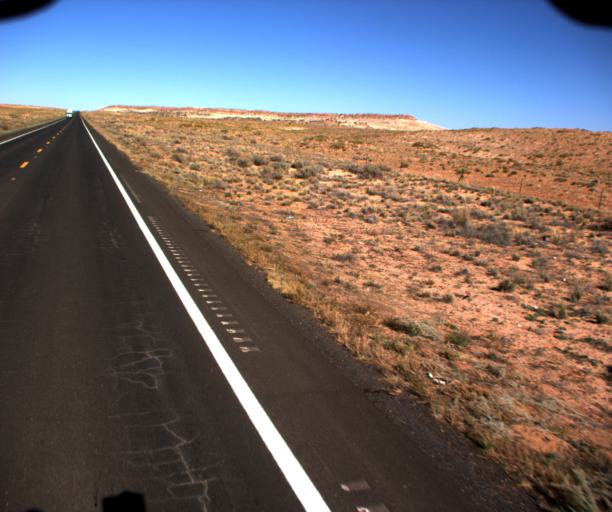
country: US
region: Arizona
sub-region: Coconino County
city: Tuba City
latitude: 36.2126
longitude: -111.0479
